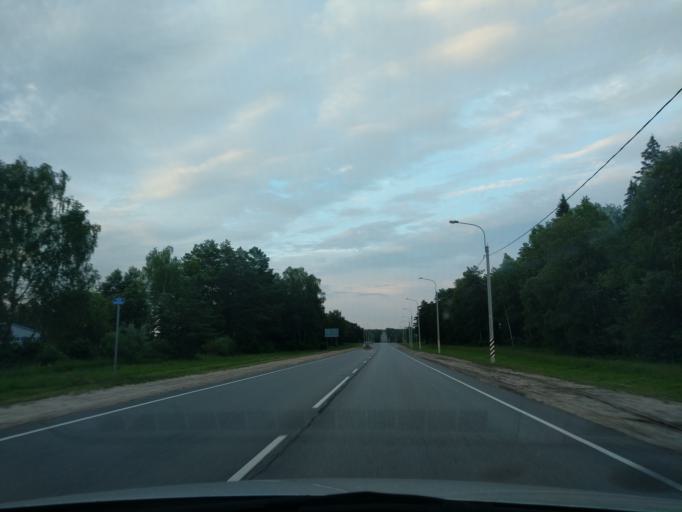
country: RU
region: Kaluga
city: Maloyaroslavets
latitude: 55.0009
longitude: 36.3978
